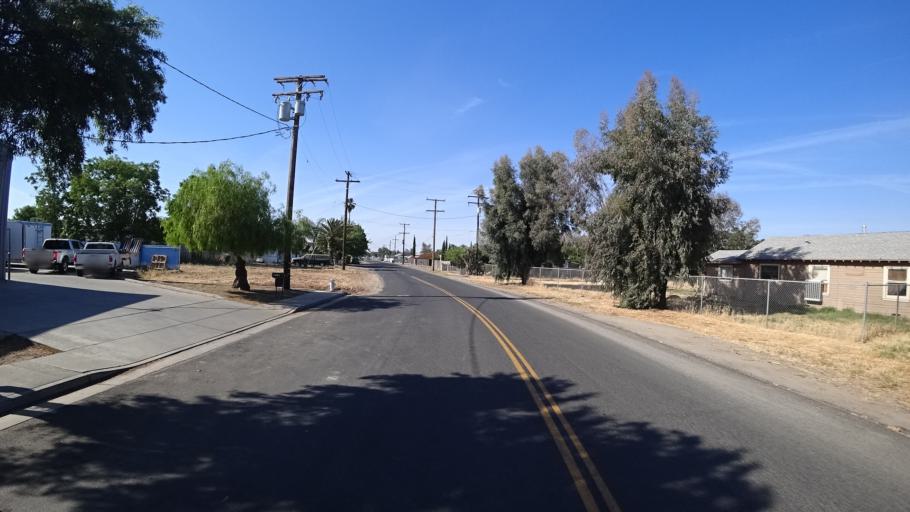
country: US
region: California
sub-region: Kings County
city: Hanford
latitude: 36.3302
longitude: -119.6345
